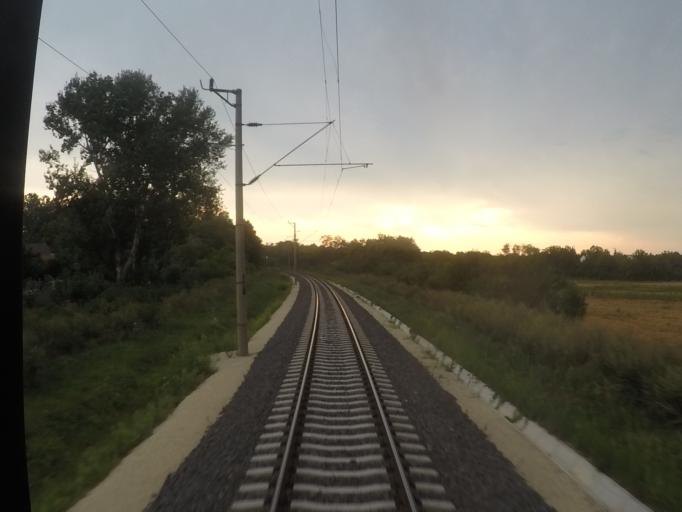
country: HU
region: Fejer
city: Lepseny
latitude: 46.9873
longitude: 18.1937
